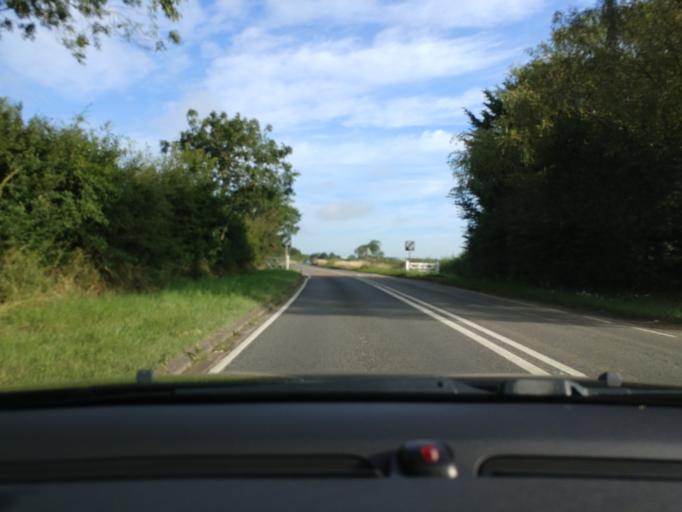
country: GB
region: England
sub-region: Oxfordshire
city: Kidlington
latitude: 51.8687
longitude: -1.2272
